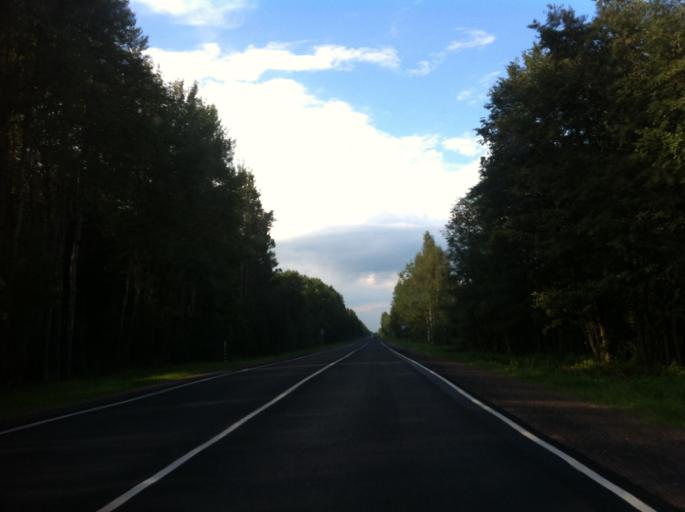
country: RU
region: Leningrad
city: Luga
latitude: 58.4918
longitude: 29.7821
